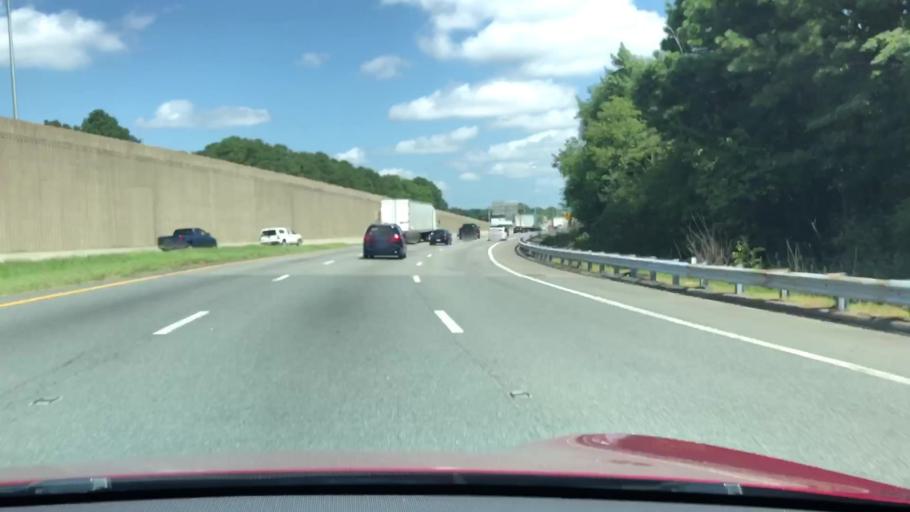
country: US
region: Virginia
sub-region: City of Chesapeake
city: Chesapeake
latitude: 36.8487
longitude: -76.1957
